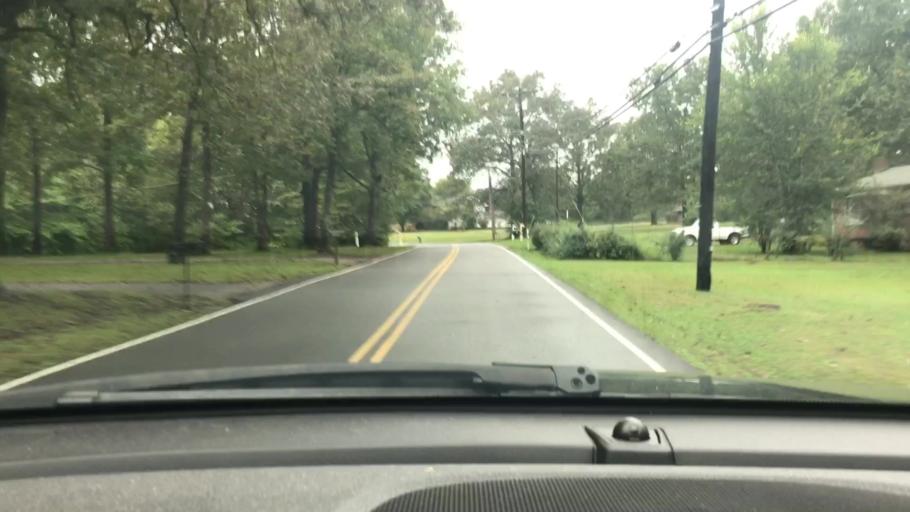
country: US
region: Tennessee
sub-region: Cheatham County
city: Kingston Springs
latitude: 36.1116
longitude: -87.1447
